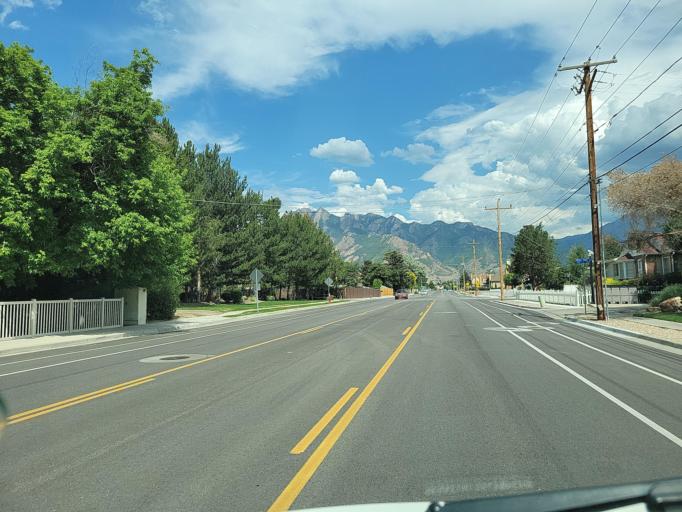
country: US
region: Utah
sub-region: Salt Lake County
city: Murray
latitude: 40.6406
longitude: -111.8600
